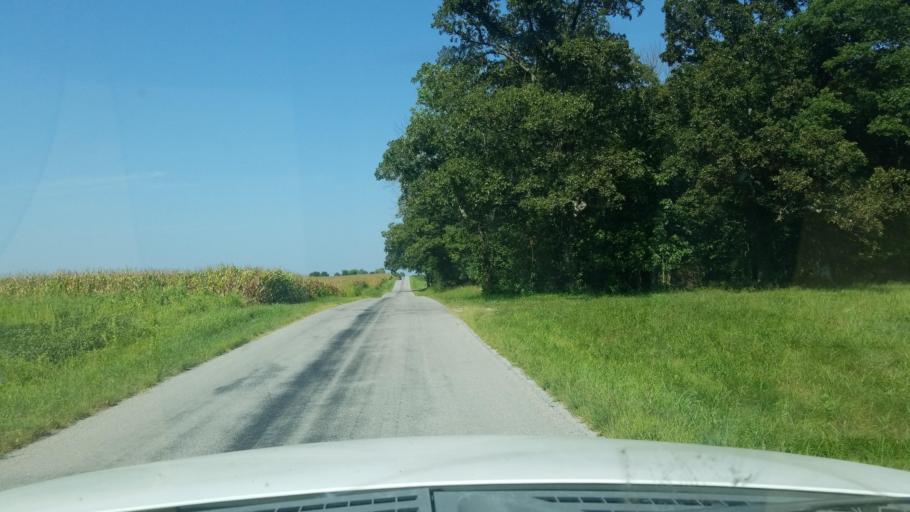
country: US
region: Illinois
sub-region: Saline County
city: Harrisburg
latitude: 37.8923
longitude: -88.6416
